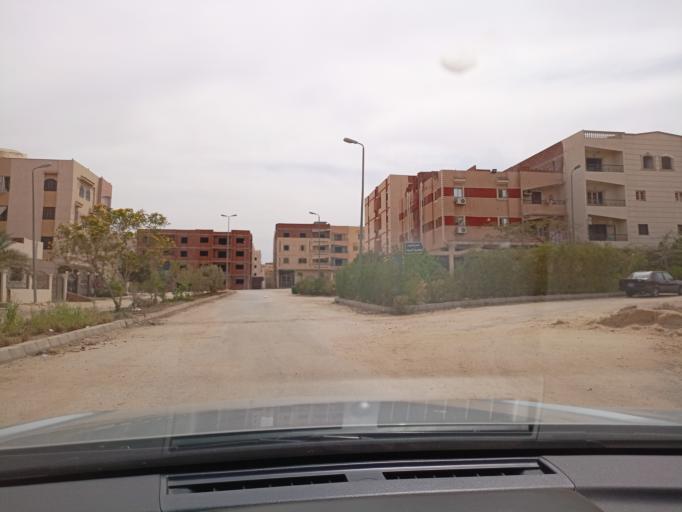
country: EG
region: Muhafazat al Qalyubiyah
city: Al Khankah
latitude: 30.2472
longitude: 31.4988
